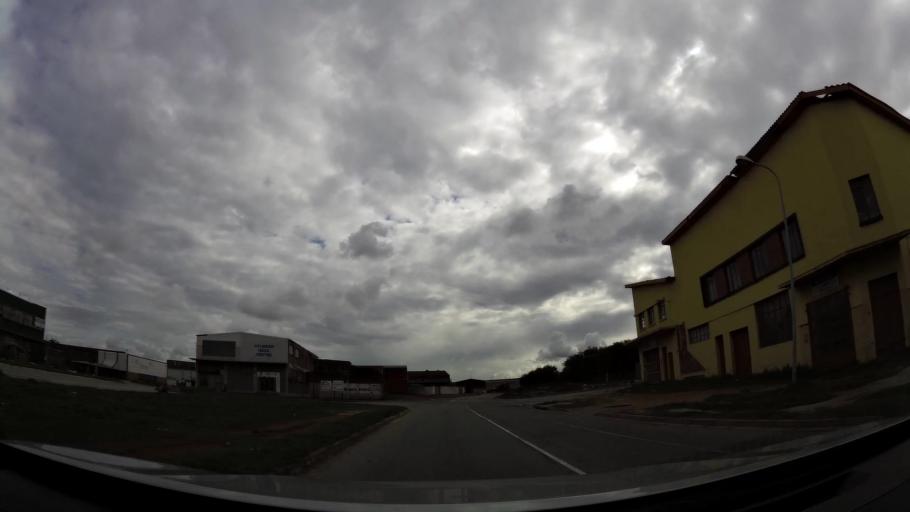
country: ZA
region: Eastern Cape
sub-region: Nelson Mandela Bay Metropolitan Municipality
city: Port Elizabeth
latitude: -33.9292
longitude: 25.5839
